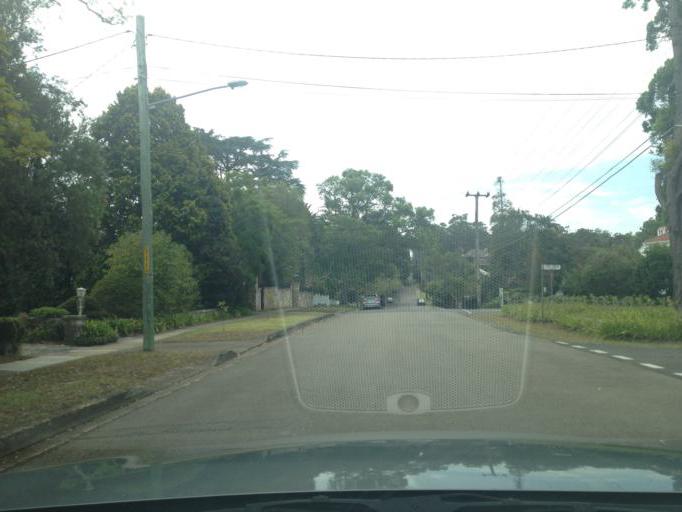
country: AU
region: New South Wales
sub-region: Ku-ring-gai
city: Killara
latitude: -33.7644
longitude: 151.1719
